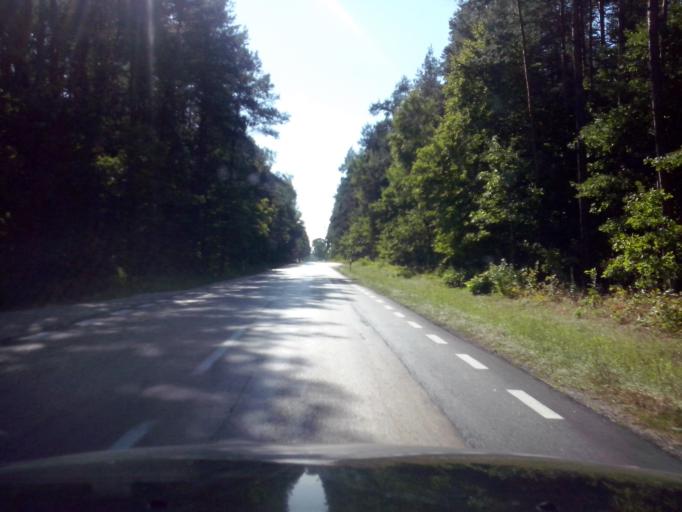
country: PL
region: Swietokrzyskie
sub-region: Powiat kielecki
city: Chmielnik
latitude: 50.6083
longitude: 20.7036
